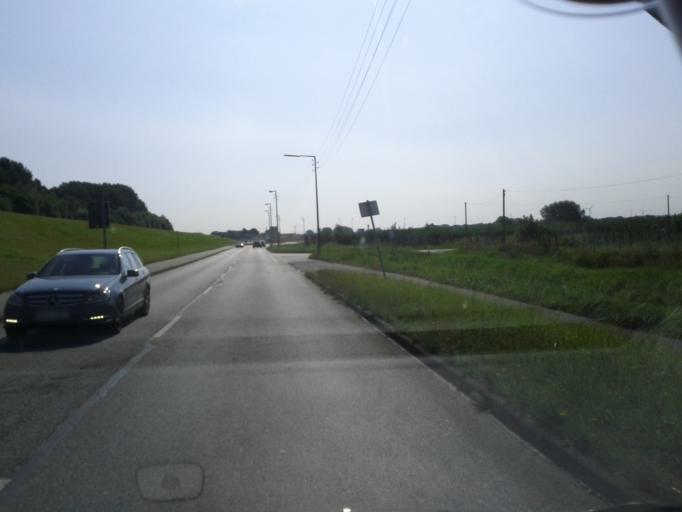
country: DE
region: Lower Saxony
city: Neu Wulmstorf
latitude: 53.5296
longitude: 9.8071
